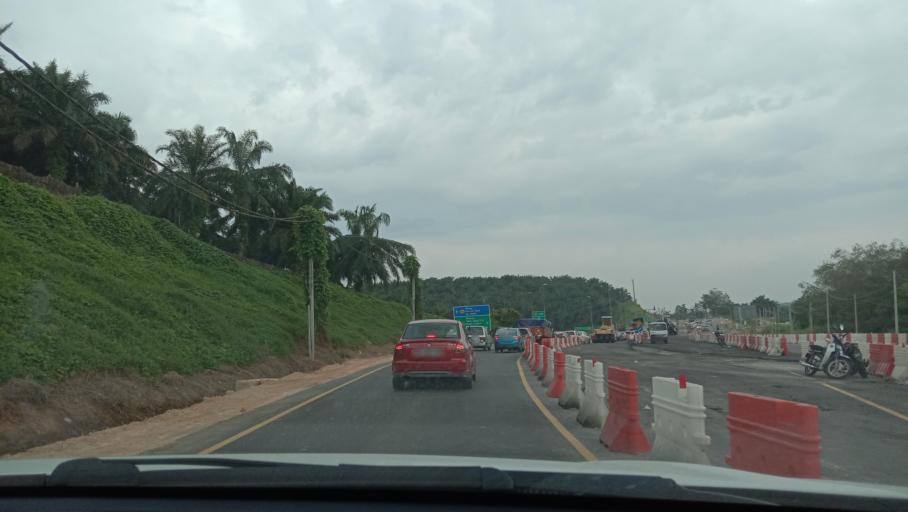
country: MY
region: Selangor
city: Batu Arang
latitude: 3.2616
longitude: 101.4630
